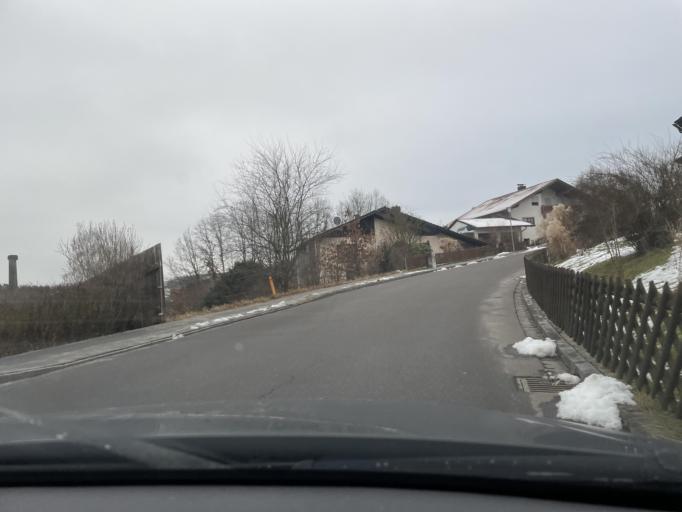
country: DE
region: Bavaria
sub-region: Lower Bavaria
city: Viechtach
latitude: 49.0750
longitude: 12.8965
